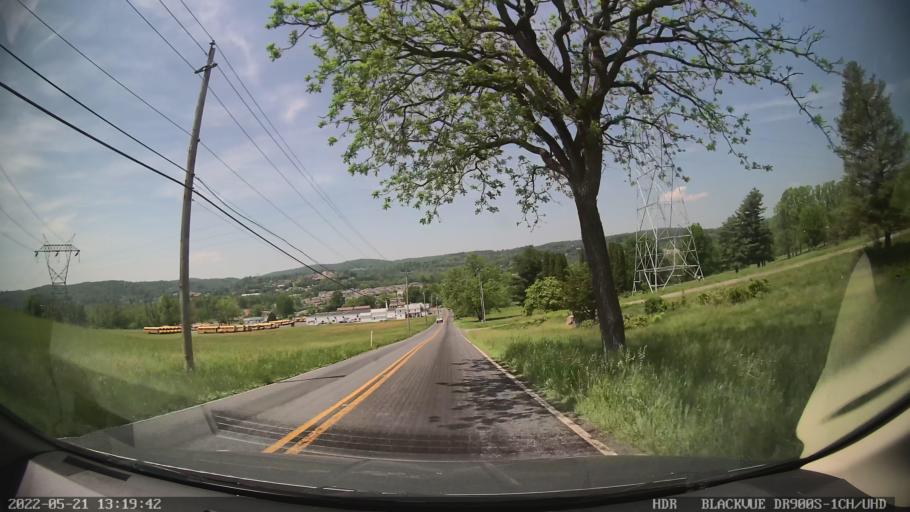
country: US
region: Pennsylvania
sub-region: Berks County
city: Bally
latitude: 40.3759
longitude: -75.6068
